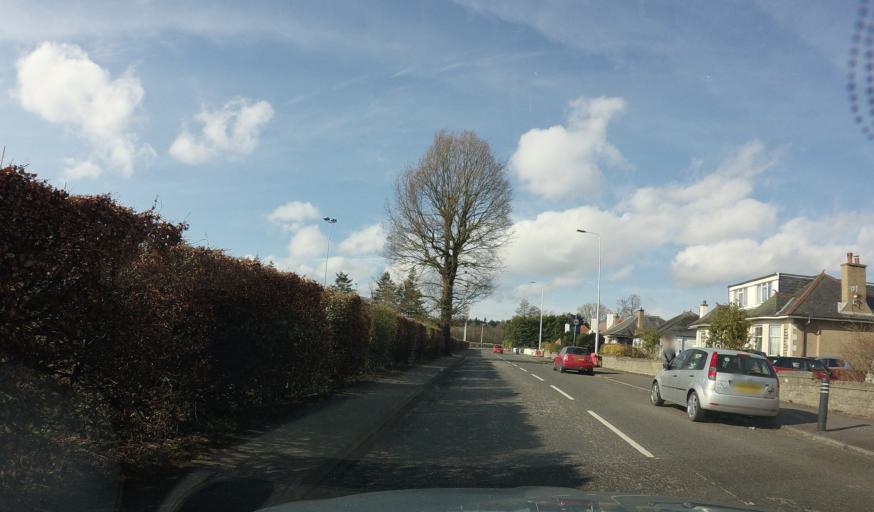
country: GB
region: Scotland
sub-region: Midlothian
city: Penicuik
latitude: 55.8301
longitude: -3.2290
